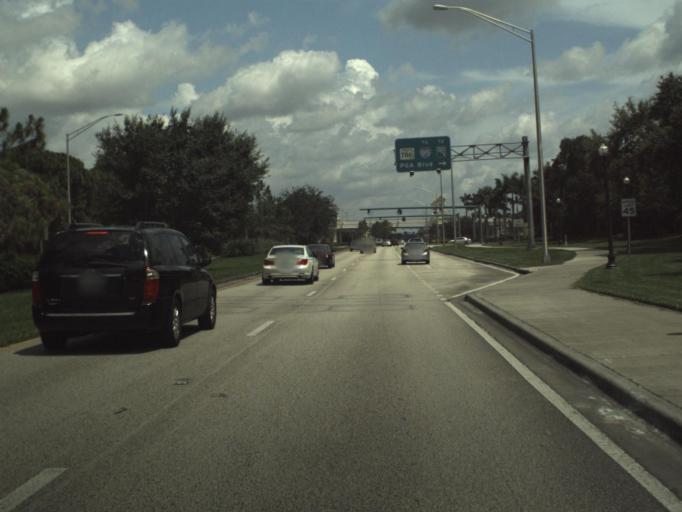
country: US
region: Florida
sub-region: Palm Beach County
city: North Palm Beach
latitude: 26.8396
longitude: -80.0939
